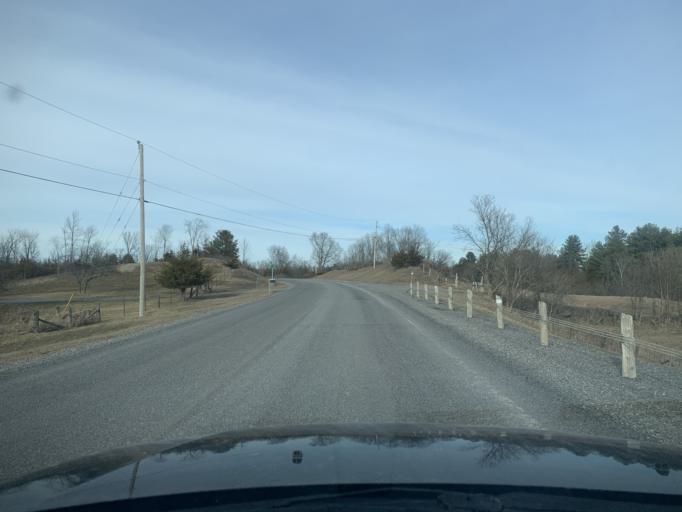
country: CA
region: Ontario
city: Greater Napanee
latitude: 44.4607
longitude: -77.0581
